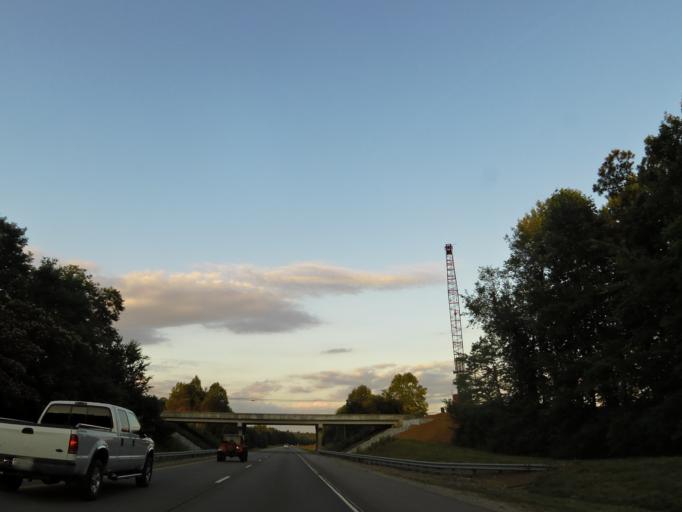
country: US
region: Tennessee
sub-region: Putnam County
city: Baxter
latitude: 36.1394
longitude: -85.5804
